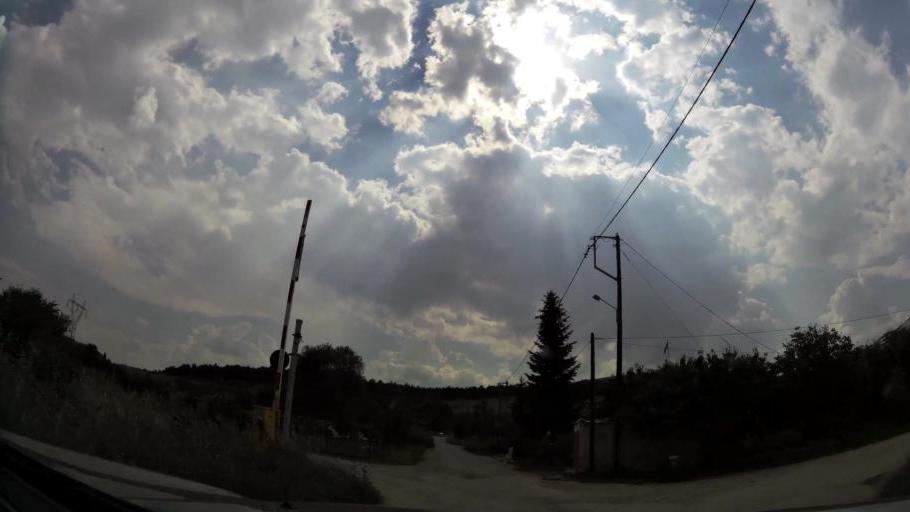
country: GR
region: West Macedonia
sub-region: Nomos Kozanis
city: Koila
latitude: 40.3478
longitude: 21.8245
